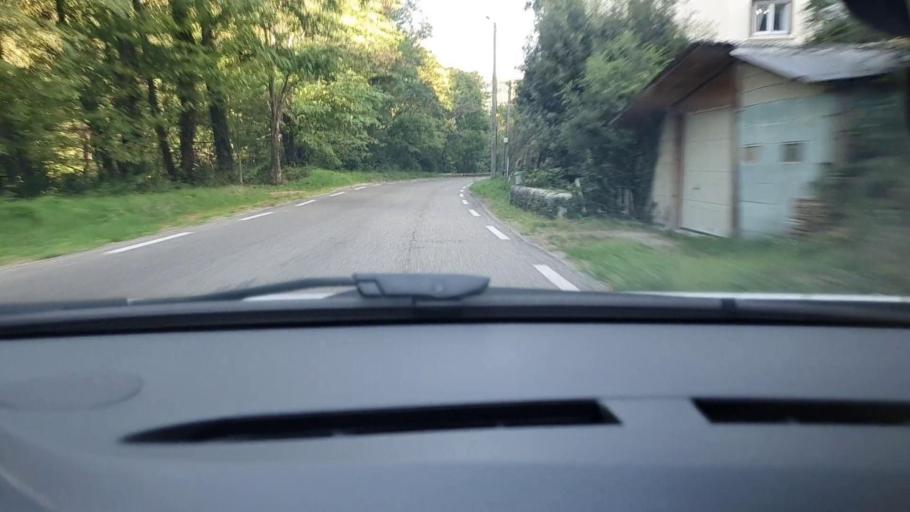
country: FR
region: Languedoc-Roussillon
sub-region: Departement du Gard
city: Besseges
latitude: 44.2932
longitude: 4.0737
